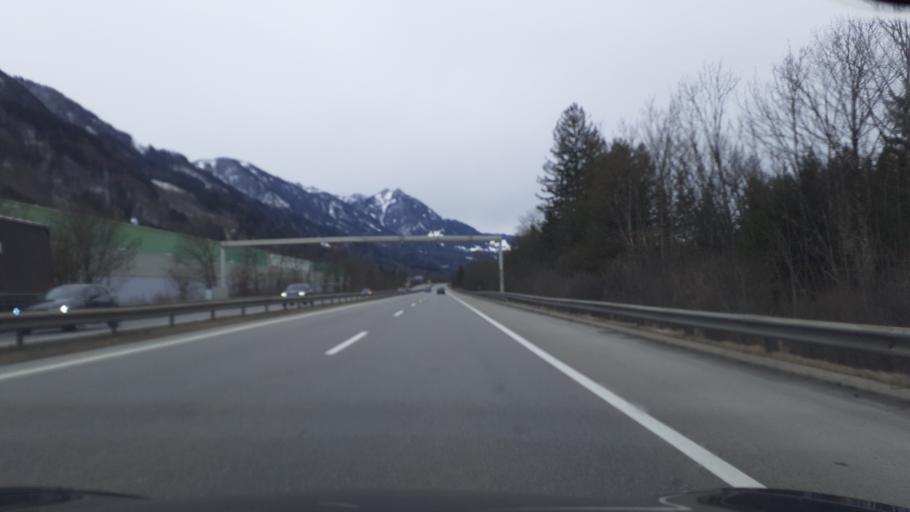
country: AT
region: Vorarlberg
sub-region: Politischer Bezirk Bludenz
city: Thuringen
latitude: 47.1756
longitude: 9.7511
